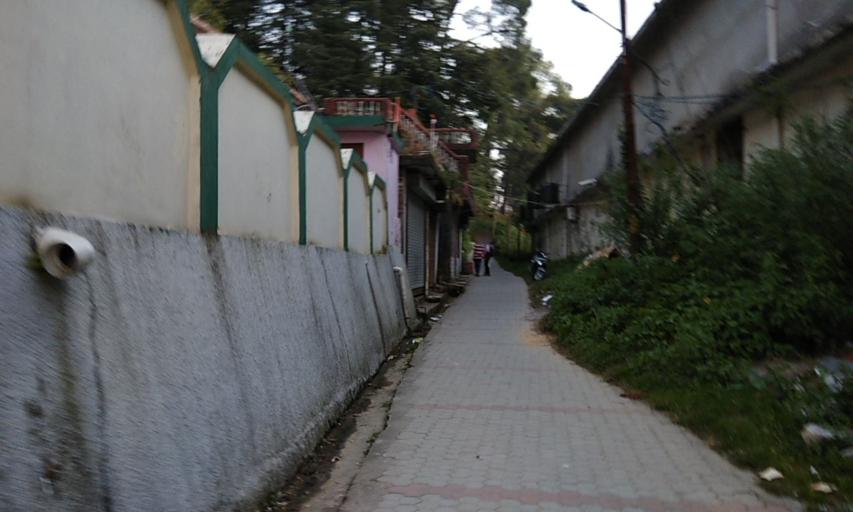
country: IN
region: Himachal Pradesh
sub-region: Kangra
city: Palampur
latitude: 32.1142
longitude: 76.5353
